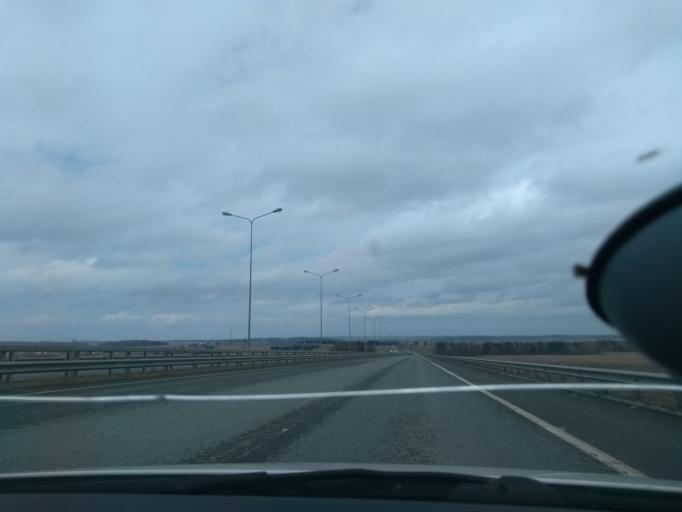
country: RU
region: Perm
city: Zvezdnyy
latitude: 57.7711
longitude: 56.3367
